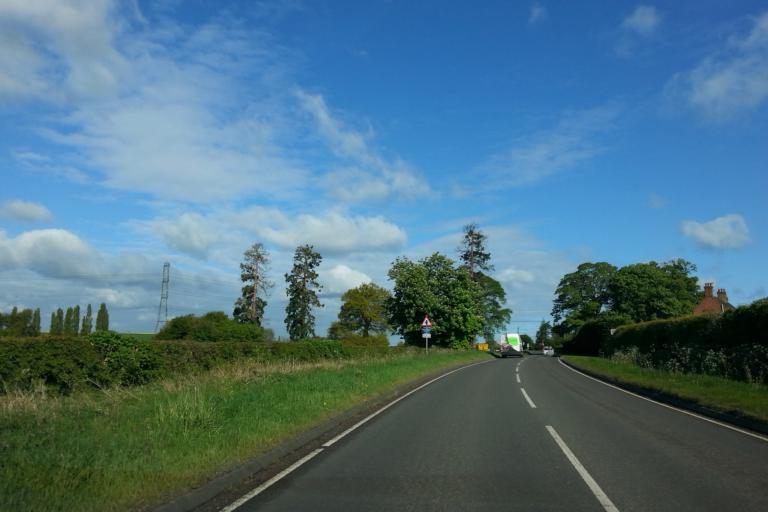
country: GB
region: England
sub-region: Nottinghamshire
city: Cotgrave
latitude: 52.9211
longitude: -1.0155
